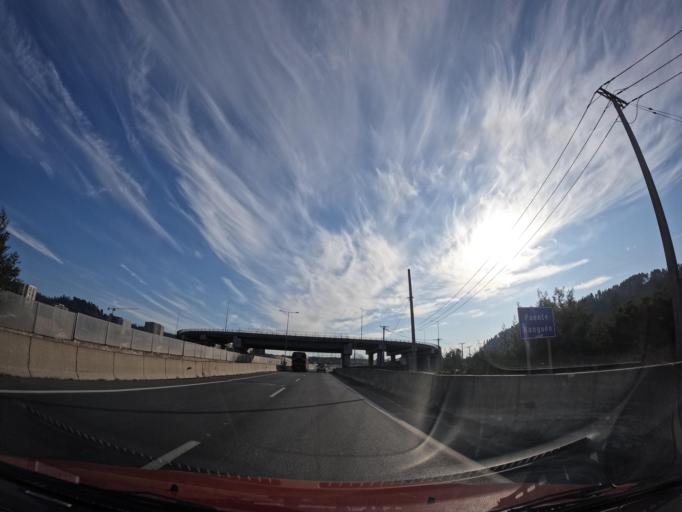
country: CL
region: Biobio
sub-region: Provincia de Concepcion
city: Concepcion
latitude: -36.8172
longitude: -73.0153
